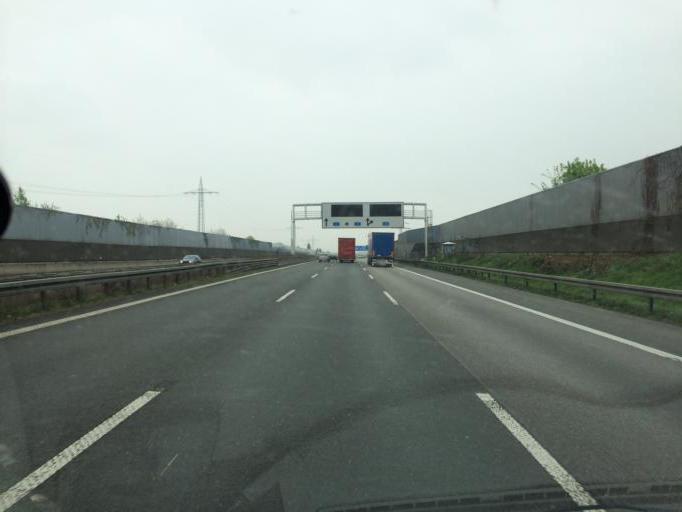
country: DE
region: North Rhine-Westphalia
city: Castrop-Rauxel
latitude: 51.5971
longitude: 7.3374
